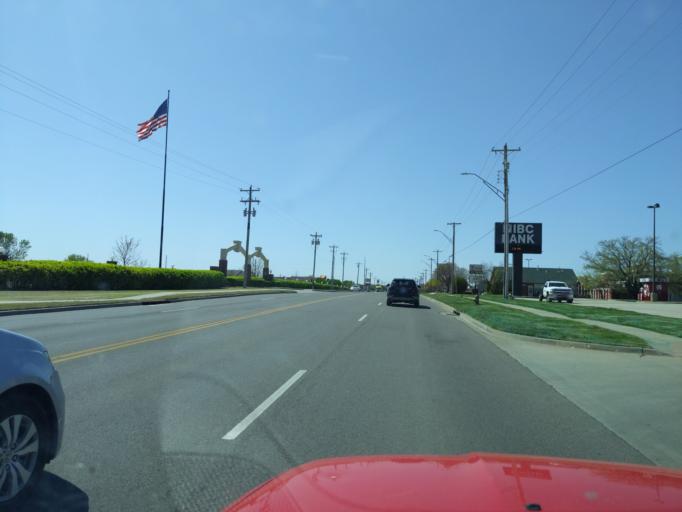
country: US
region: Oklahoma
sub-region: Cleveland County
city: Moore
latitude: 35.3199
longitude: -97.5072
